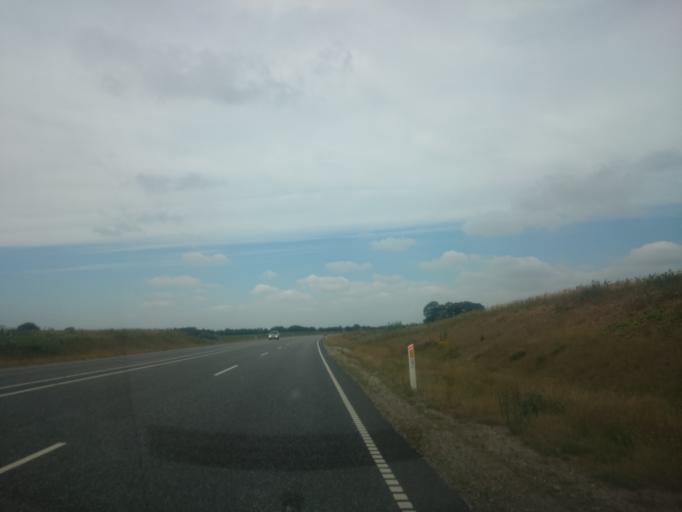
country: DK
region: South Denmark
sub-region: Vejle Kommune
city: Egtved
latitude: 55.6961
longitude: 9.3274
